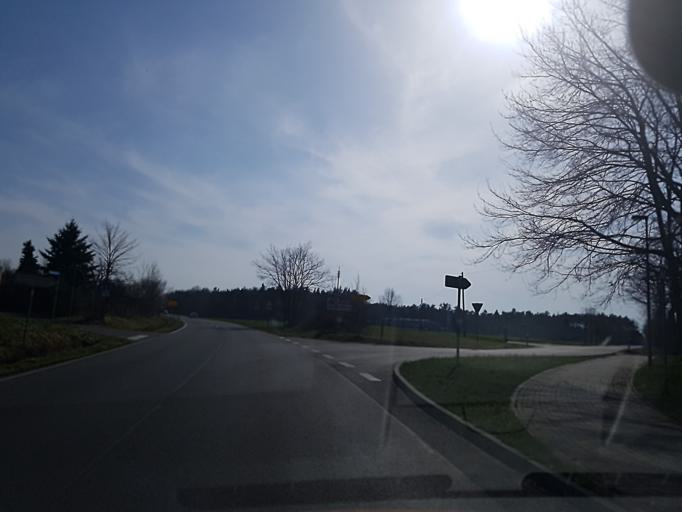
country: DE
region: Brandenburg
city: Calau
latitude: 51.7421
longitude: 13.9402
